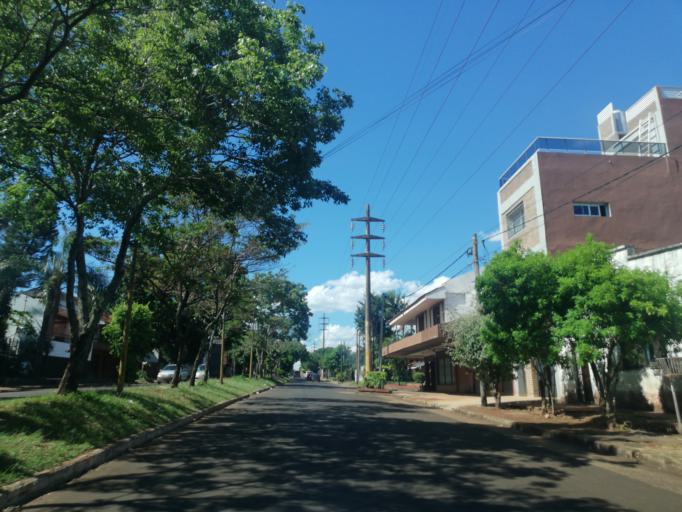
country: AR
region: Misiones
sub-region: Departamento de Capital
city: Posadas
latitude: -27.3898
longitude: -55.8931
